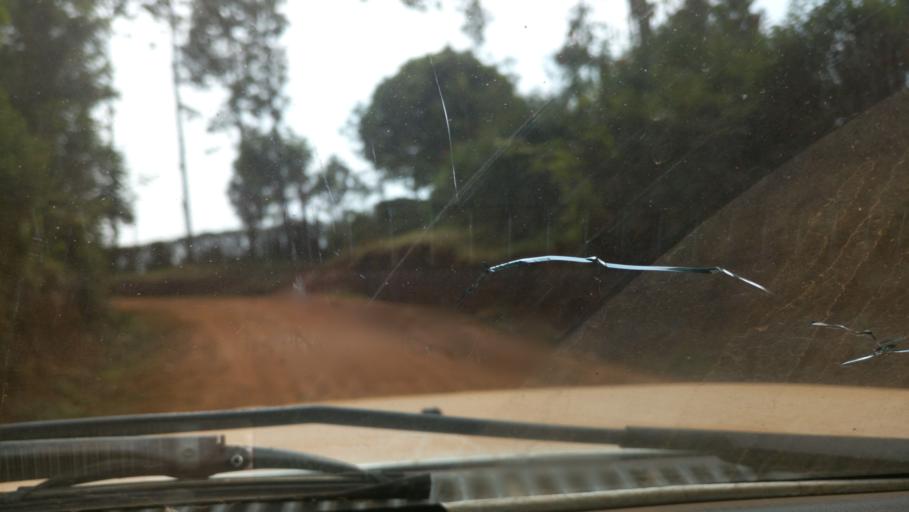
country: KE
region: Murang'a District
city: Kangema
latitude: -0.7341
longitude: 36.9910
